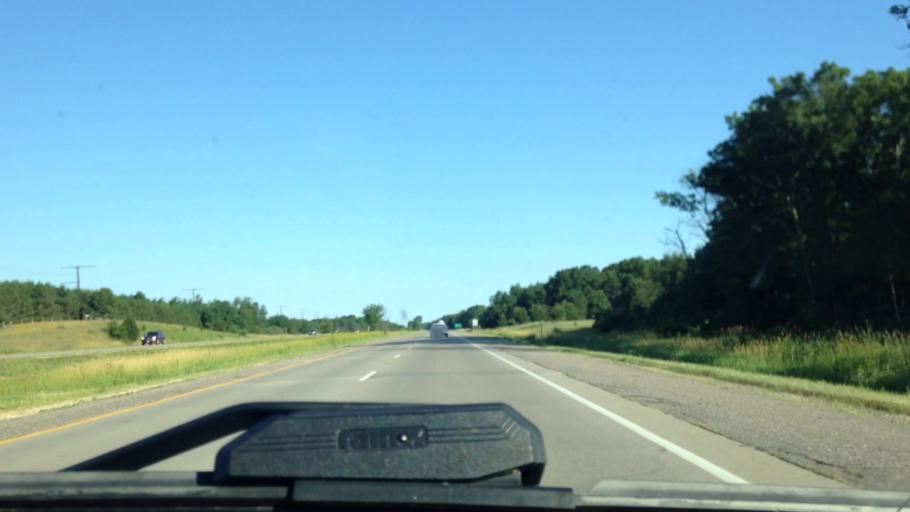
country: US
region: Wisconsin
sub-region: Columbia County
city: Wisconsin Dells
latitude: 43.7231
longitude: -89.9026
